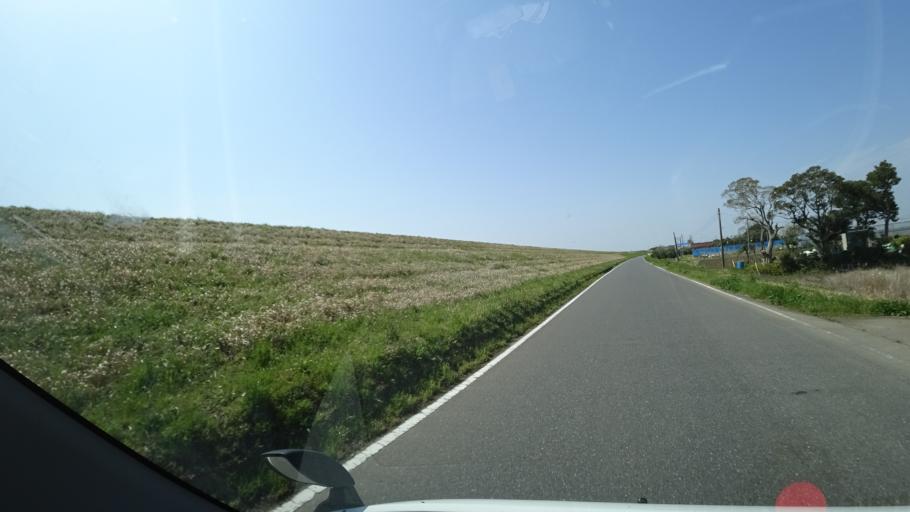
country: JP
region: Ibaraki
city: Edosaki
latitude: 35.8693
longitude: 140.3228
